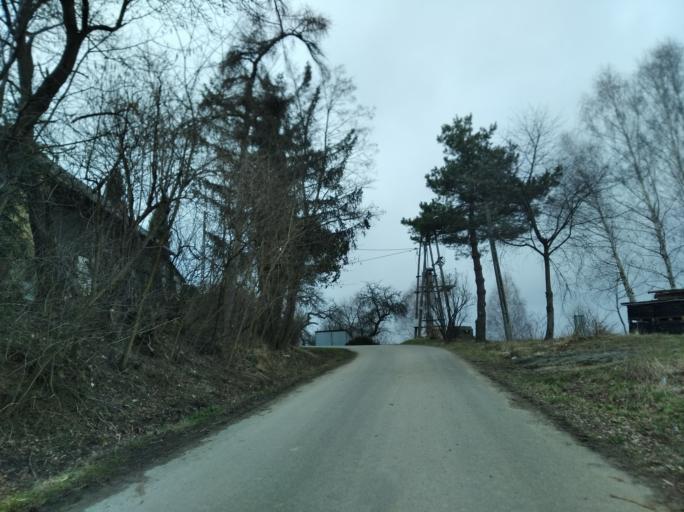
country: PL
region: Subcarpathian Voivodeship
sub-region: Powiat strzyzowski
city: Strzyzow
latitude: 49.8798
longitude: 21.8039
